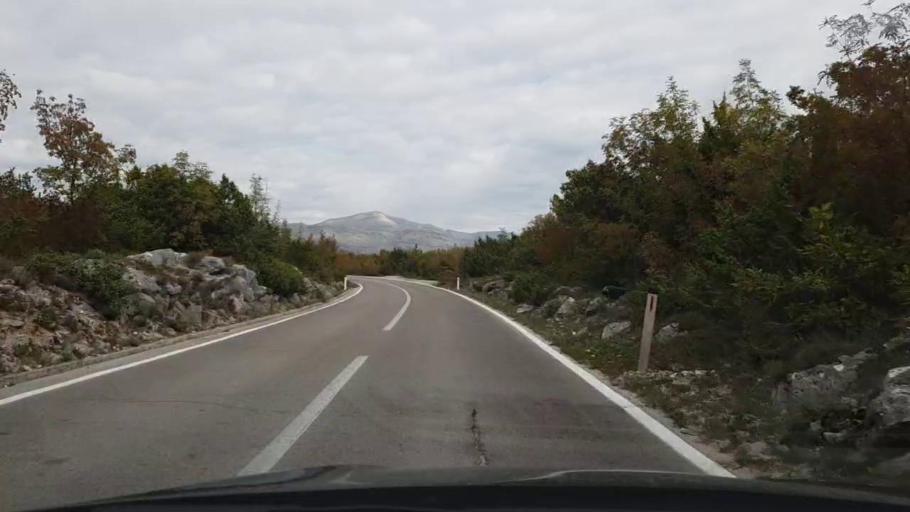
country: HR
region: Dubrovacko-Neretvanska
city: Cibaca
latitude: 42.6749
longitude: 18.2341
